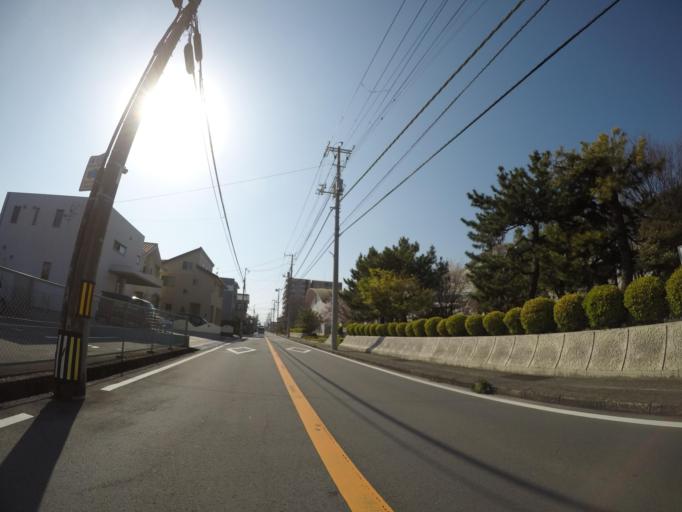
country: JP
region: Shizuoka
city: Numazu
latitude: 35.1030
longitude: 138.8498
